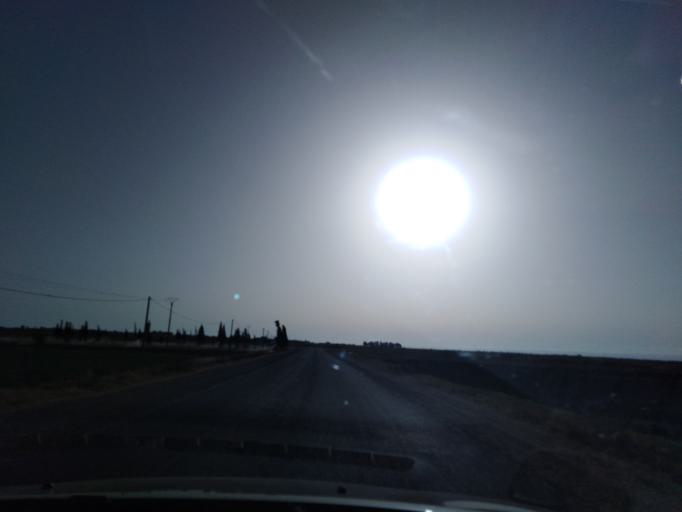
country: MA
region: Doukkala-Abda
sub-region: Safi
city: Safi
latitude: 32.4783
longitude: -8.8856
